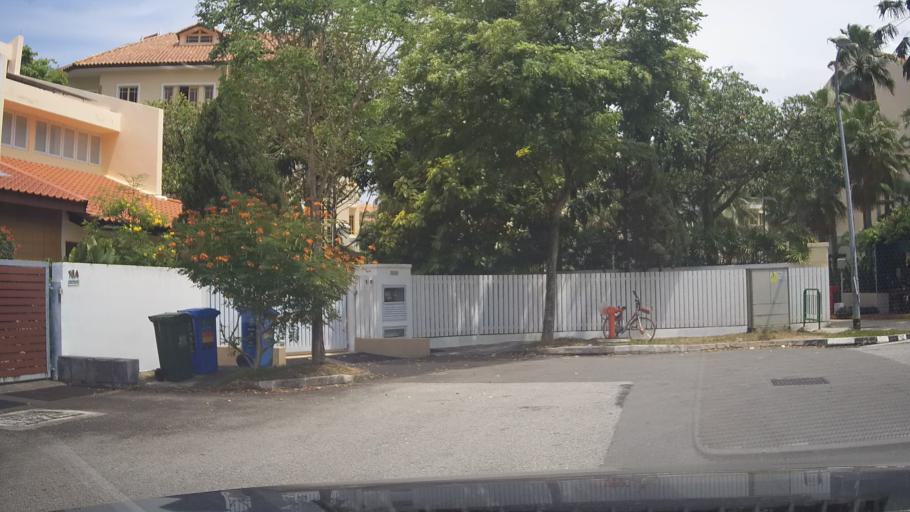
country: SG
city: Singapore
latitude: 1.3103
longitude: 103.9265
